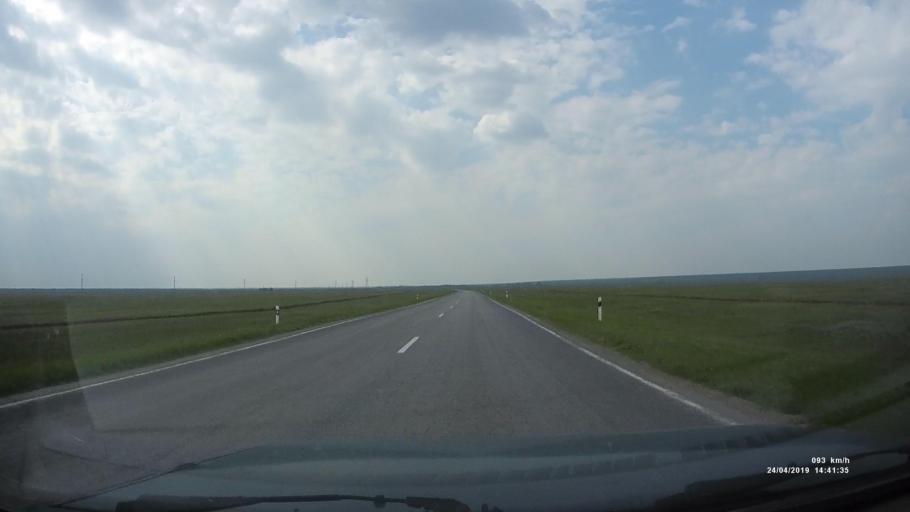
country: RU
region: Rostov
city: Remontnoye
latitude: 46.4465
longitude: 43.8774
